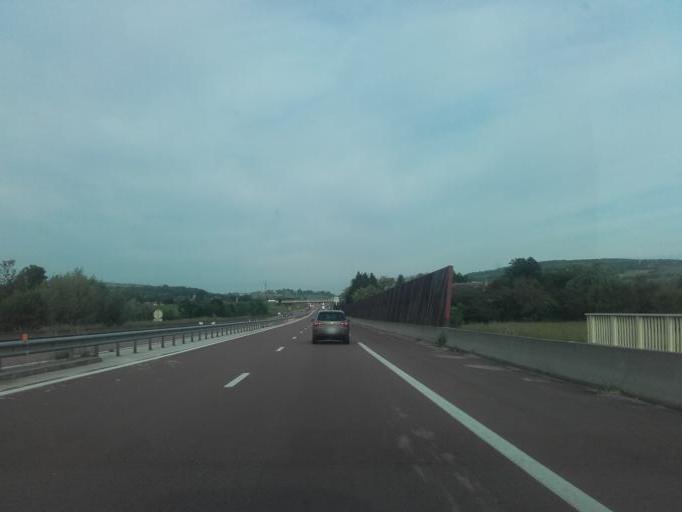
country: FR
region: Bourgogne
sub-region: Departement de Saone-et-Loire
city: Givry
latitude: 46.7585
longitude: 4.7282
